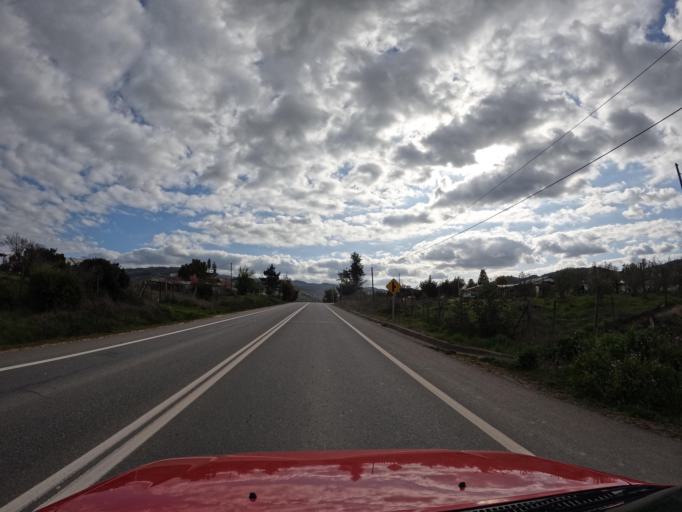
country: CL
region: Maule
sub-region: Provincia de Talca
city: Constitucion
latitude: -35.5565
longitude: -72.1237
